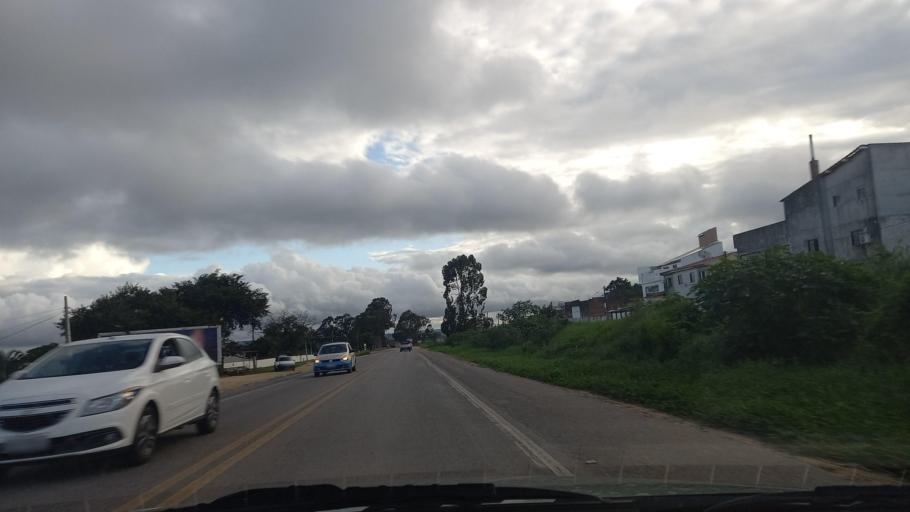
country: BR
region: Pernambuco
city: Garanhuns
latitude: -8.9093
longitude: -36.4901
